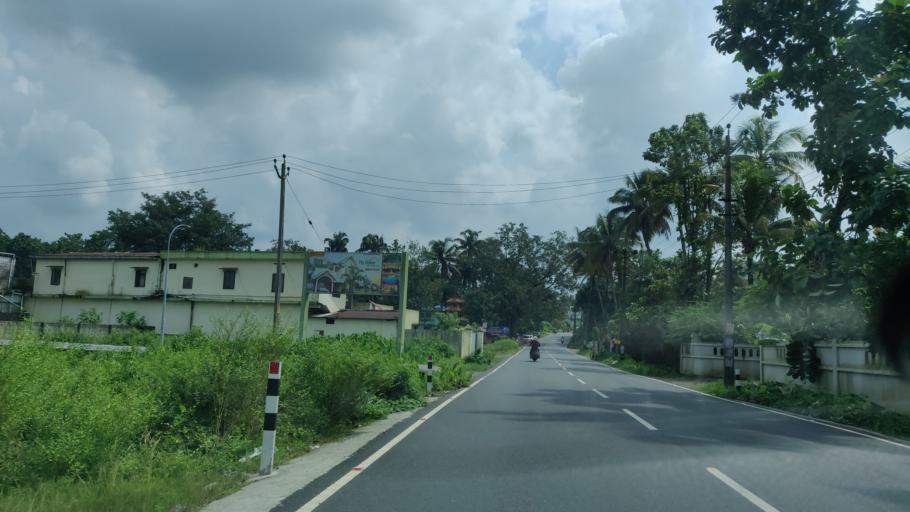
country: IN
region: Kerala
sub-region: Ernakulam
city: Angamali
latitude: 10.1684
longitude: 76.4208
